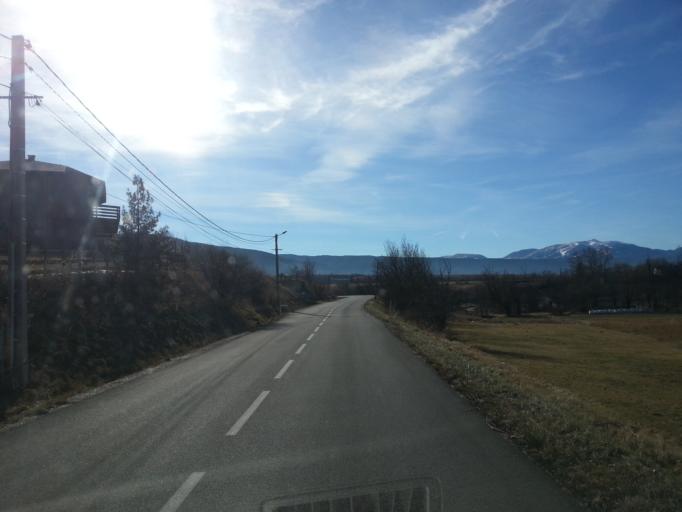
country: ES
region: Catalonia
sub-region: Provincia de Girona
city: Llivia
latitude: 42.4649
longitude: 2.0078
